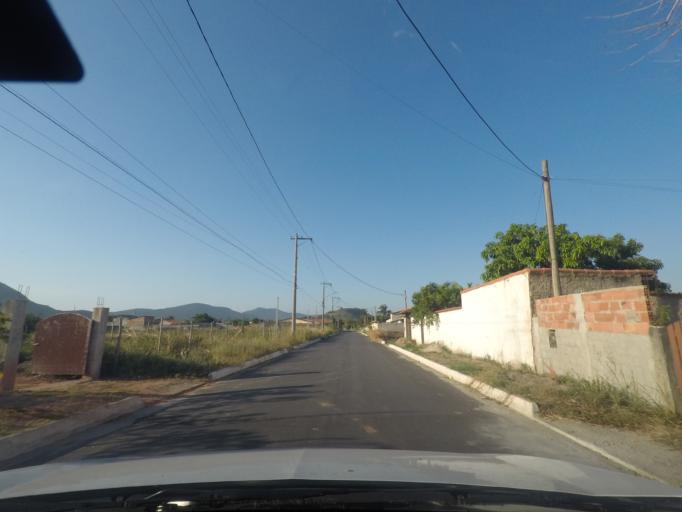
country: BR
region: Rio de Janeiro
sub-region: Marica
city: Marica
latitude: -22.9584
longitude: -42.9352
